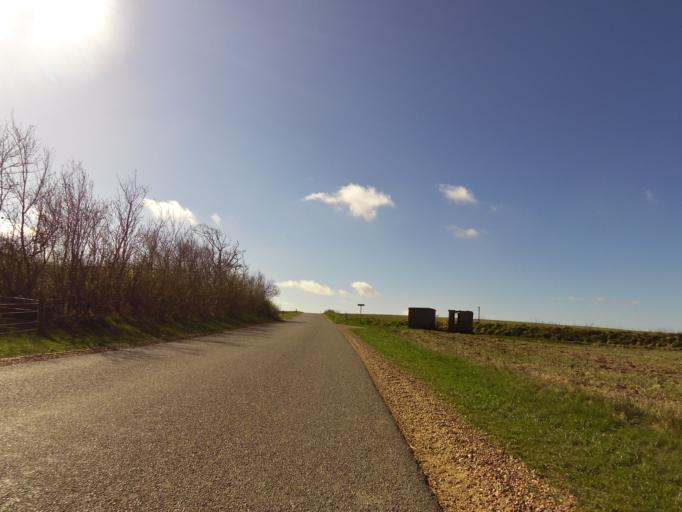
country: DK
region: Central Jutland
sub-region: Holstebro Kommune
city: Vinderup
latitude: 56.4645
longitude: 8.7215
